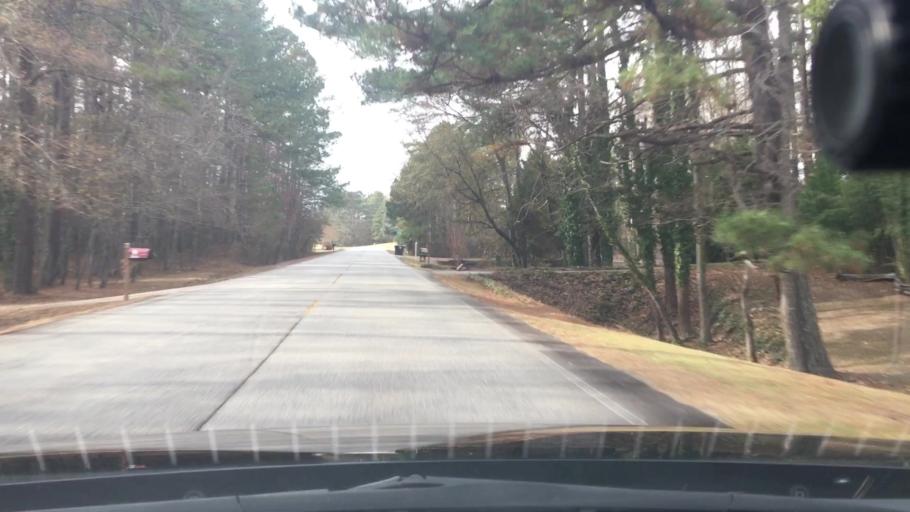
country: US
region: Georgia
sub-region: Coweta County
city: Senoia
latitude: 33.2873
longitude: -84.4429
